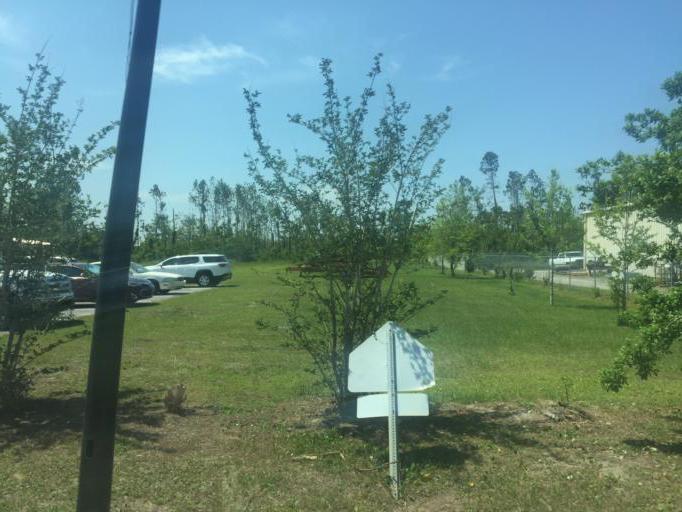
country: US
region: Florida
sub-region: Bay County
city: Hiland Park
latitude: 30.2113
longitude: -85.6469
